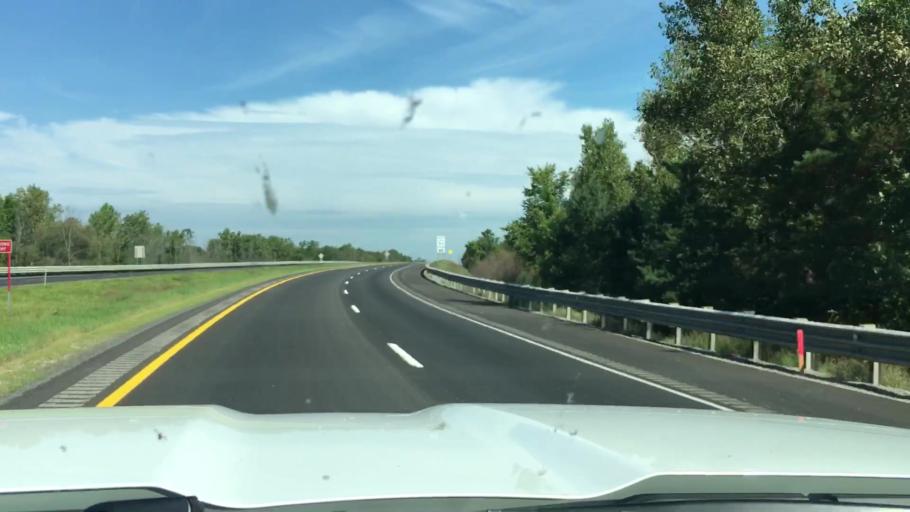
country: US
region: Michigan
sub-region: Saginaw County
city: Freeland
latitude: 43.5395
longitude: -84.1386
